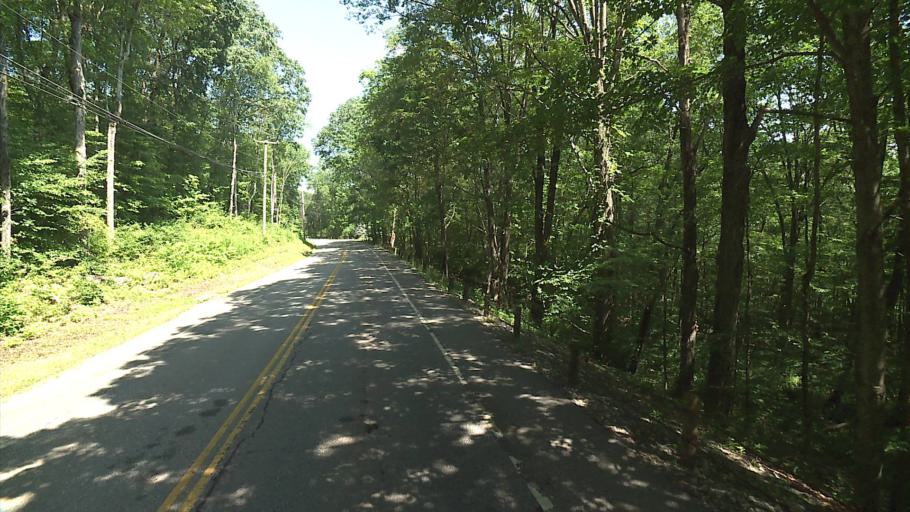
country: US
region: Connecticut
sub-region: Litchfield County
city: New Preston
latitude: 41.7365
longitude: -73.3386
